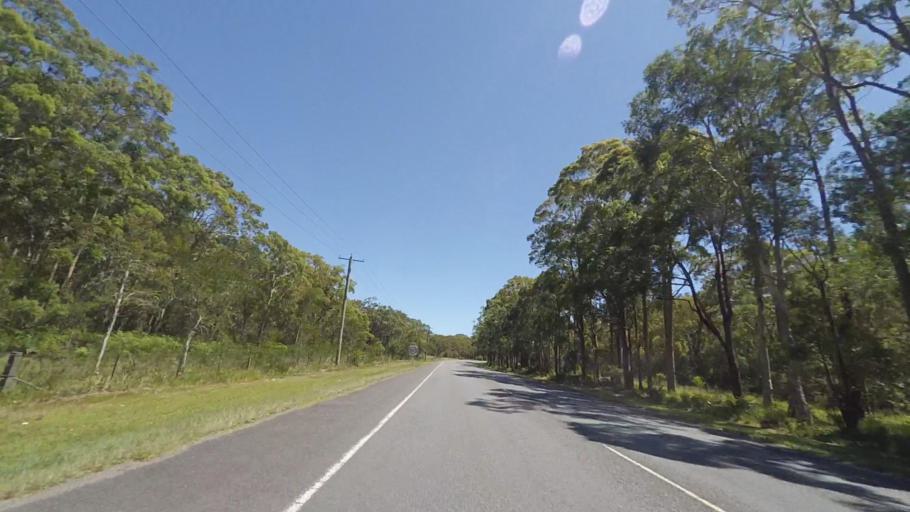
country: AU
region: New South Wales
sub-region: Port Stephens Shire
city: Medowie
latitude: -32.7779
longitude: 151.8590
